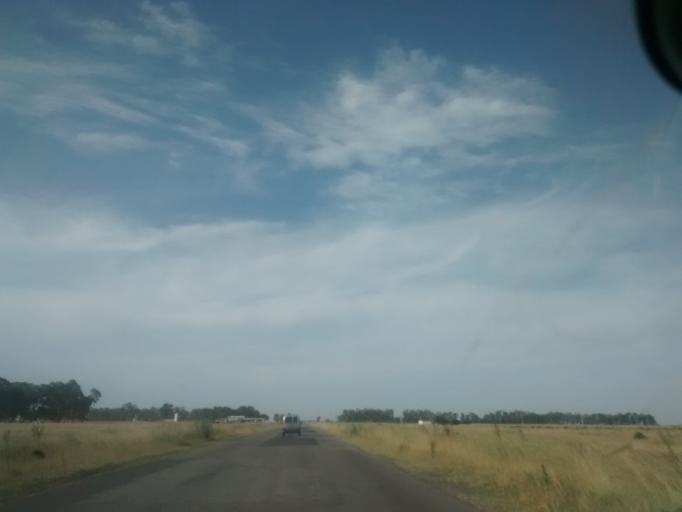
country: AR
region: Buenos Aires
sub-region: Partido de Ayacucho
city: Ayacucho
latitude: -37.1392
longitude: -58.5533
